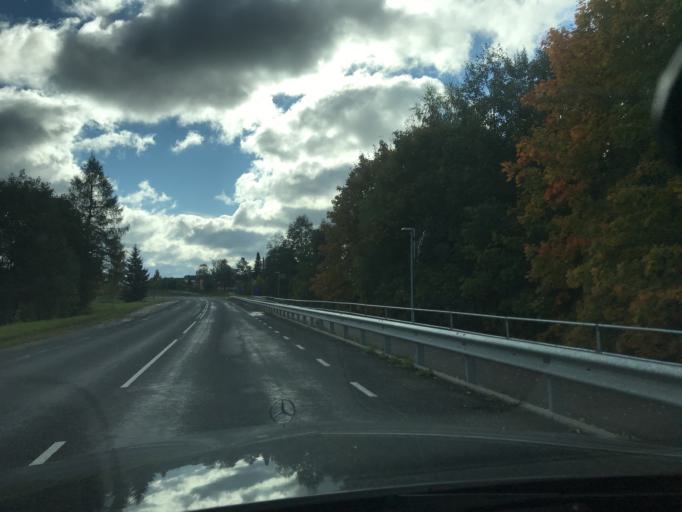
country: EE
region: Vorumaa
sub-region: Antsla vald
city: Vana-Antsla
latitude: 57.9571
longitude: 26.2755
